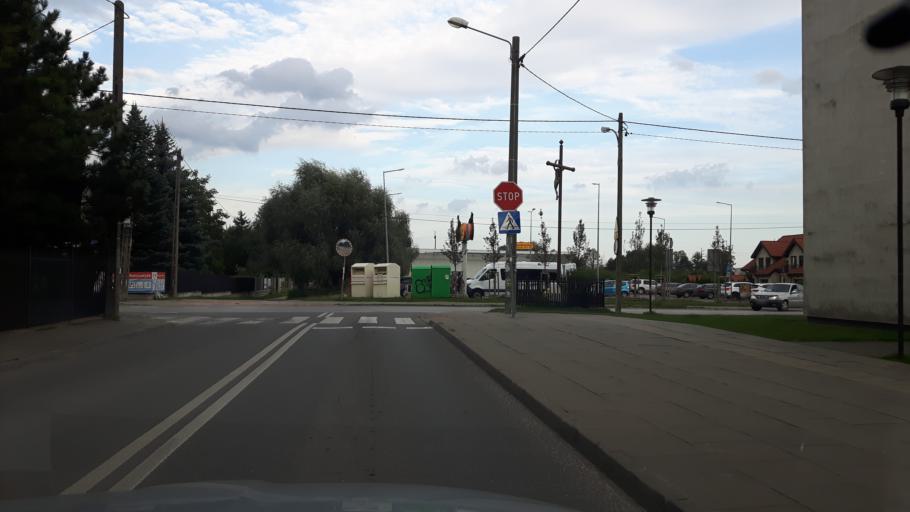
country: PL
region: Masovian Voivodeship
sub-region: Warszawa
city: Targowek
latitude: 52.3178
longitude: 21.0499
